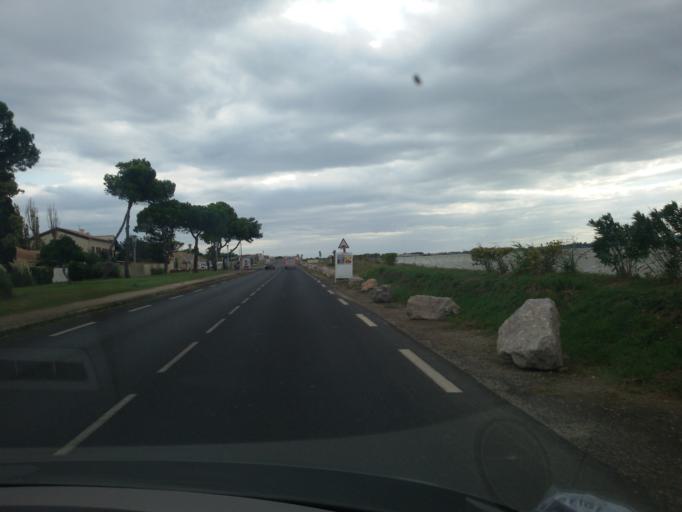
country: FR
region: Languedoc-Roussillon
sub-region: Departement de l'Herault
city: Palavas-les-Flots
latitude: 43.5280
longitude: 3.9213
